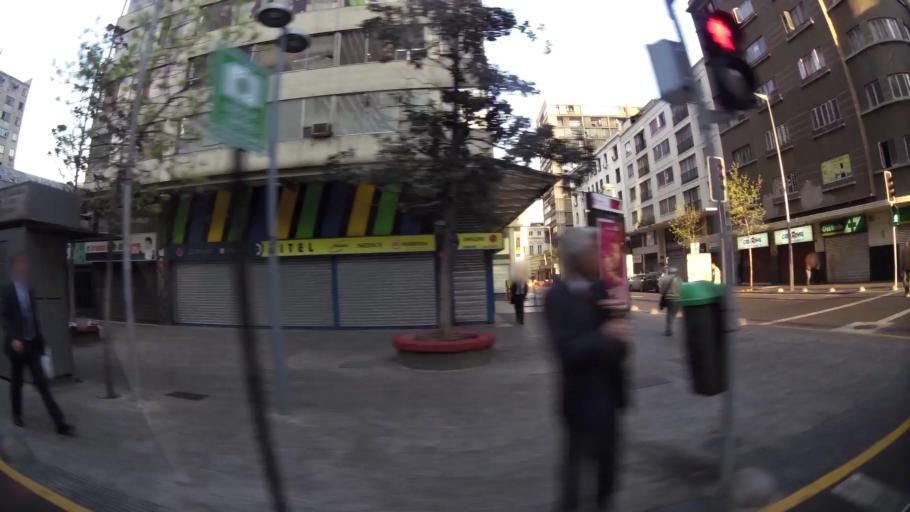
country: CL
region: Santiago Metropolitan
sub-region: Provincia de Santiago
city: Santiago
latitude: -33.4372
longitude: -70.6486
